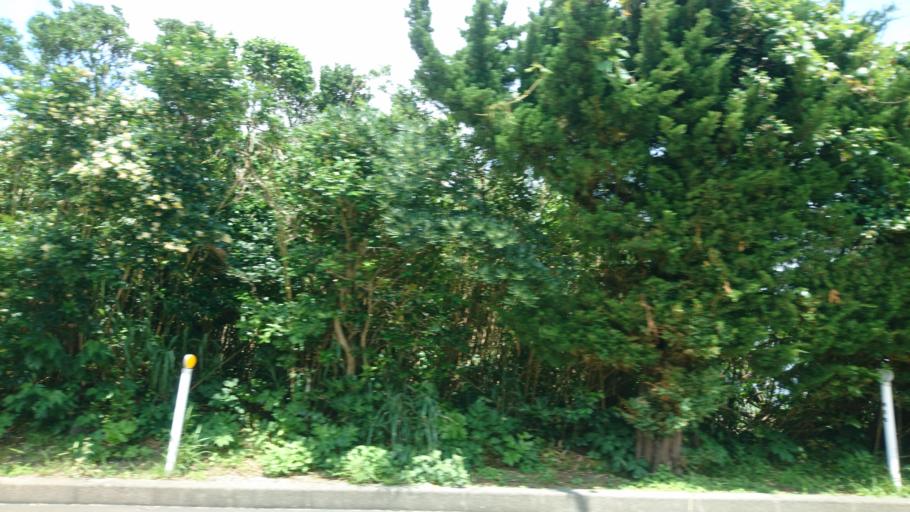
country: JP
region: Shizuoka
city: Shimoda
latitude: 34.4119
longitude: 139.2805
